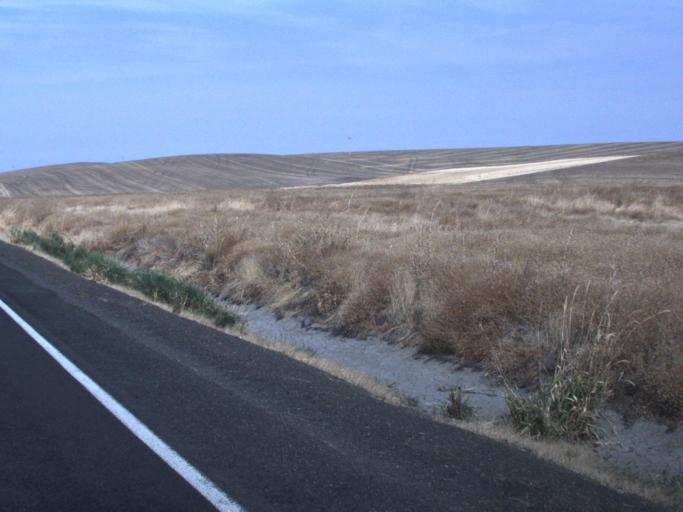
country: US
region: Idaho
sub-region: Benewah County
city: Plummer
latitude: 47.1939
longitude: -117.1156
